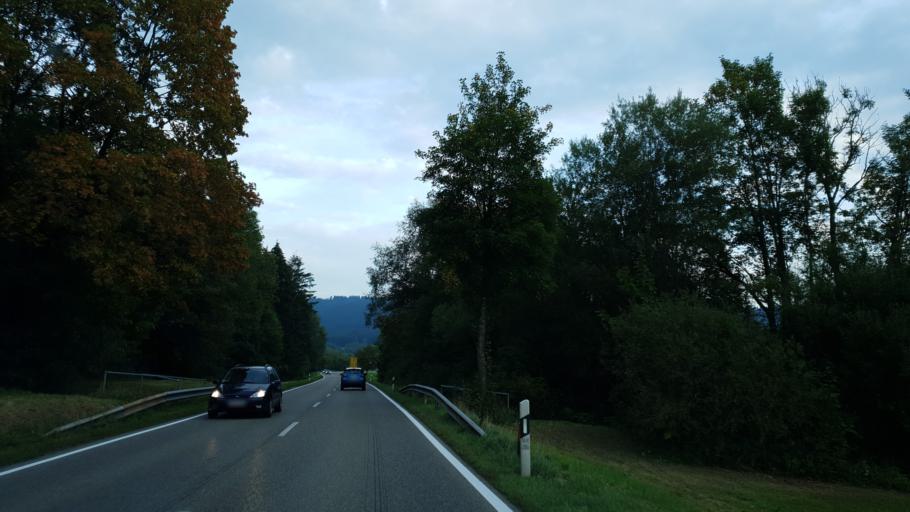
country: DE
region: Bavaria
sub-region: Swabia
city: Maierhofen
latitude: 47.6742
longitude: 10.0911
